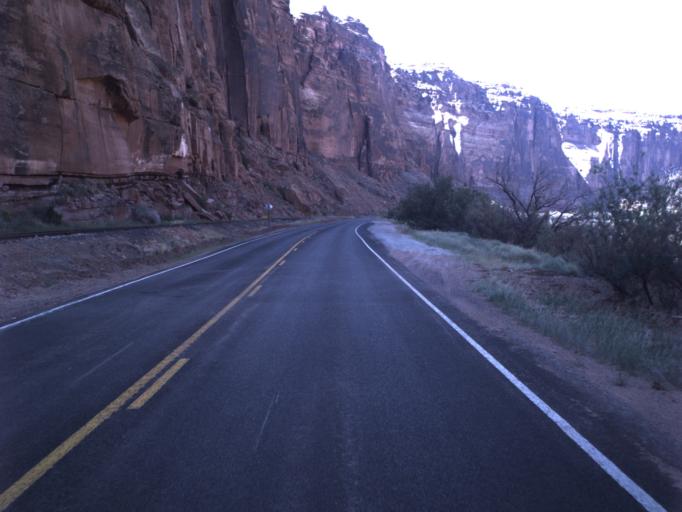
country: US
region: Utah
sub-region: Grand County
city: Moab
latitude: 38.5542
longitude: -109.6514
